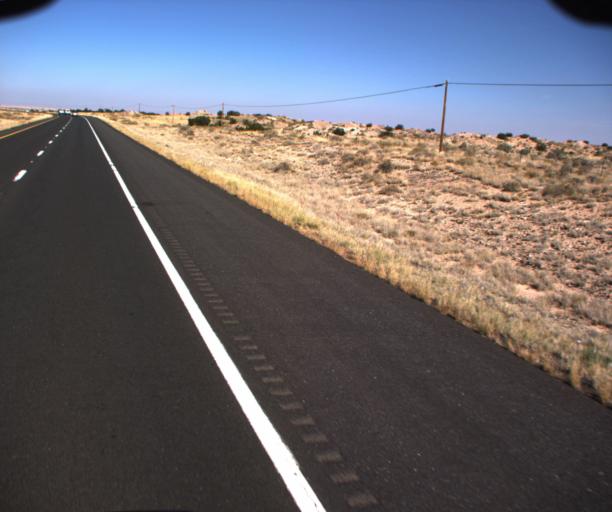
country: US
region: Arizona
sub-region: Coconino County
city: Flagstaff
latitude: 35.5132
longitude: -111.5452
